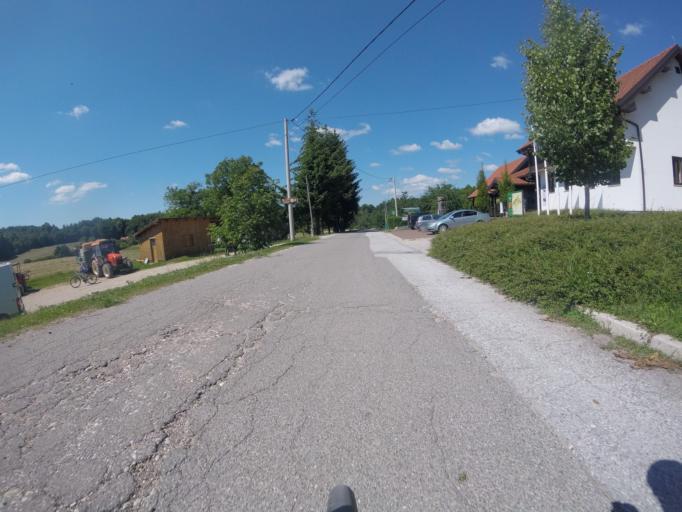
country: SI
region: Kostanjevica na Krki
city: Kostanjevica na Krki
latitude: 45.7912
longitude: 15.4931
